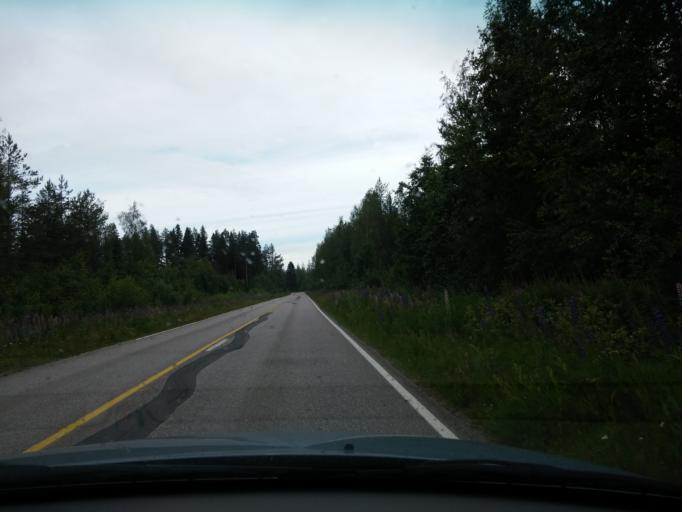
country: FI
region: Central Finland
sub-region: Saarijaervi-Viitasaari
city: Saarijaervi
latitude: 62.7431
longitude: 25.3319
